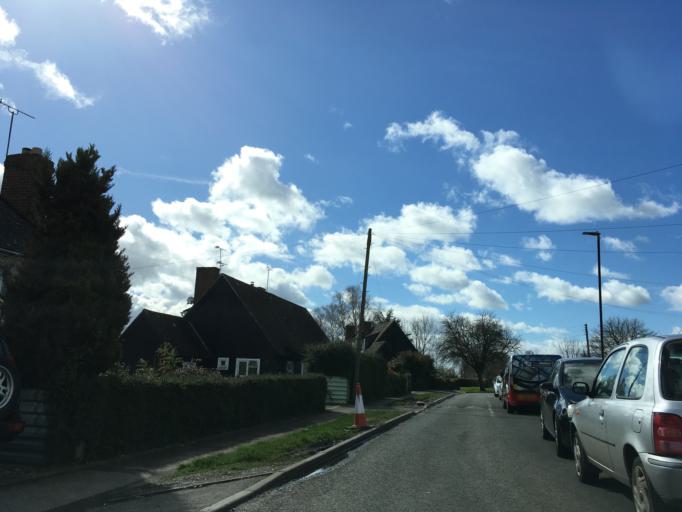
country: GB
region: England
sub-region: Gloucestershire
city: Wotton-under-Edge
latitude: 51.6358
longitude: -2.3454
